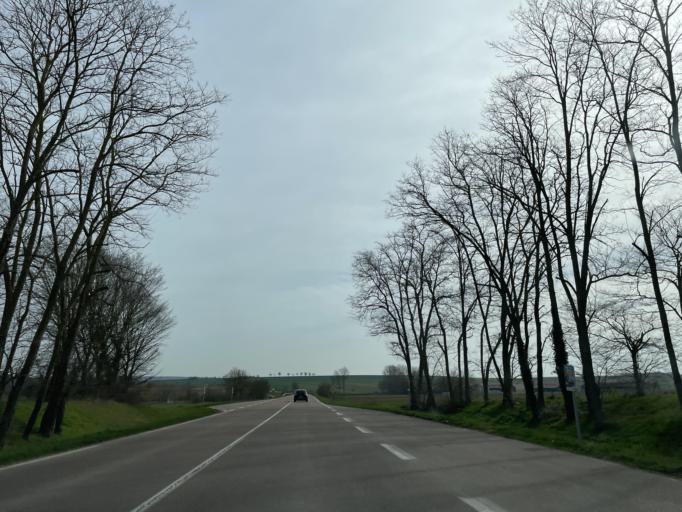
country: FR
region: Champagne-Ardenne
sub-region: Departement de l'Aube
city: Nogent-sur-Seine
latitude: 48.4826
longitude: 3.4946
